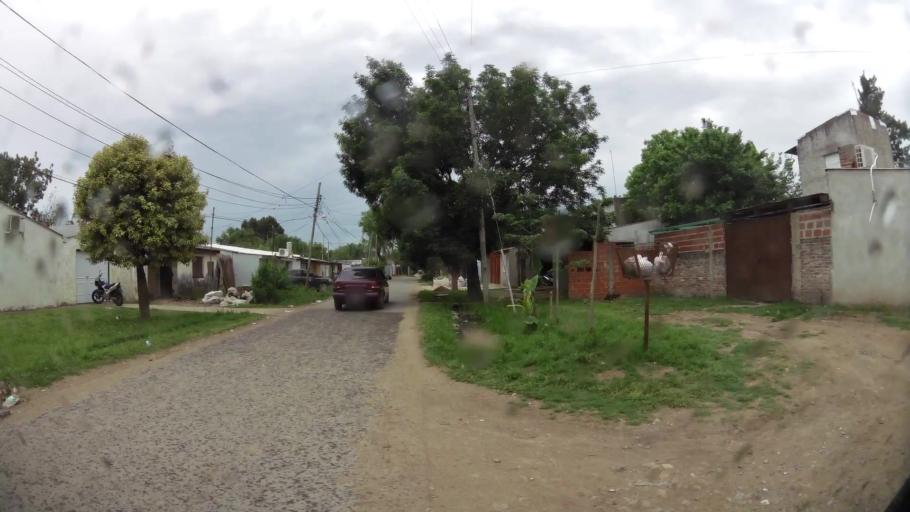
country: AR
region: Buenos Aires
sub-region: Partido de Zarate
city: Zarate
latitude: -34.1136
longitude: -59.0420
